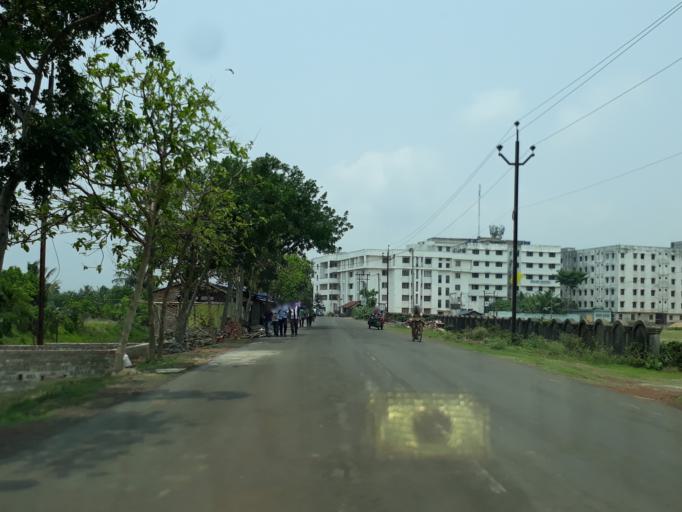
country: IN
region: West Bengal
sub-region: Purba Medinipur
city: Haldia
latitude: 22.0492
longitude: 88.0692
